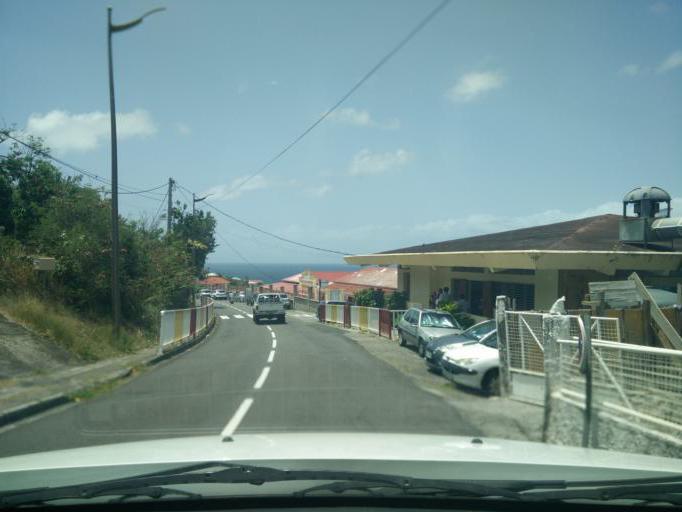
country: GP
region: Guadeloupe
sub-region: Guadeloupe
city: Gourbeyre
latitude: 15.9491
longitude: -61.7020
